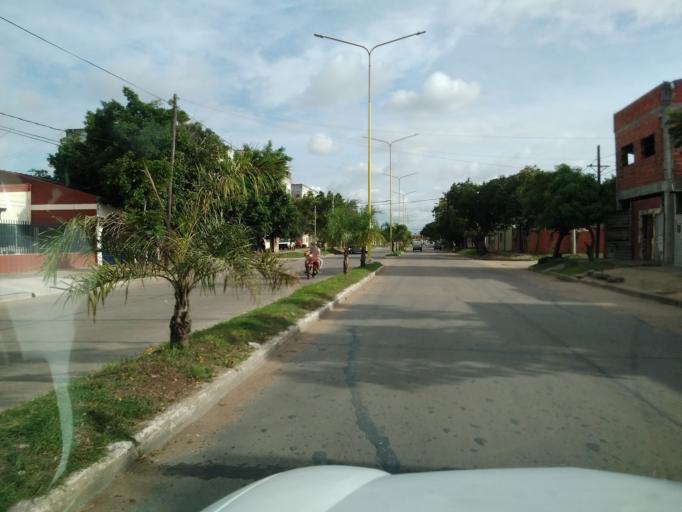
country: AR
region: Corrientes
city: Corrientes
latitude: -27.4642
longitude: -58.7884
